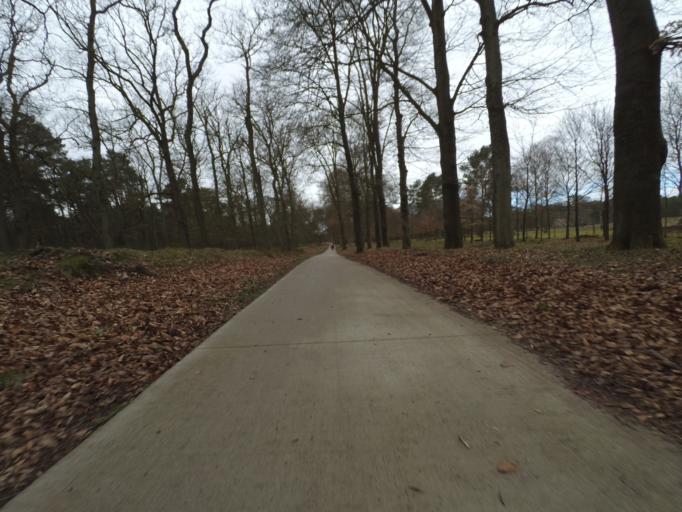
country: NL
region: Gelderland
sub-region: Gemeente Apeldoorn
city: Loenen
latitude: 52.0651
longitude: 5.9994
